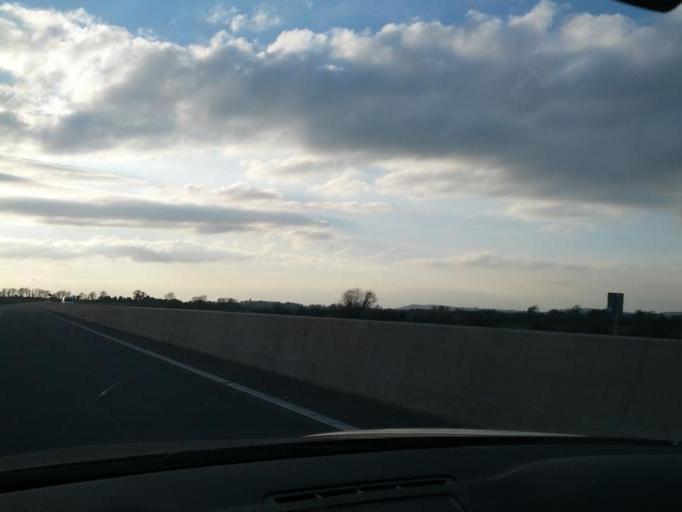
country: IE
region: Munster
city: Nenagh Bridge
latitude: 52.8746
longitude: -8.0313
